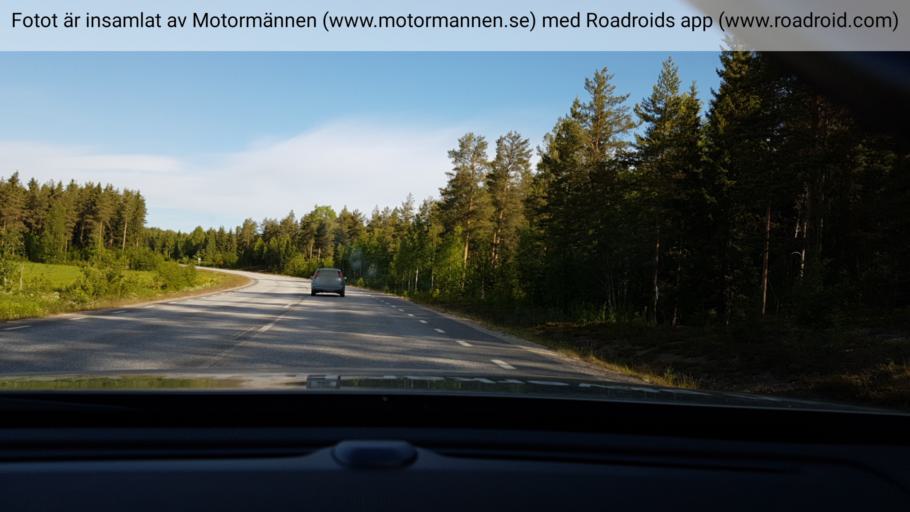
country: SE
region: Vaesterbotten
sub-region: Vannas Kommun
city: Vaennaes
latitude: 64.0050
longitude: 19.7185
